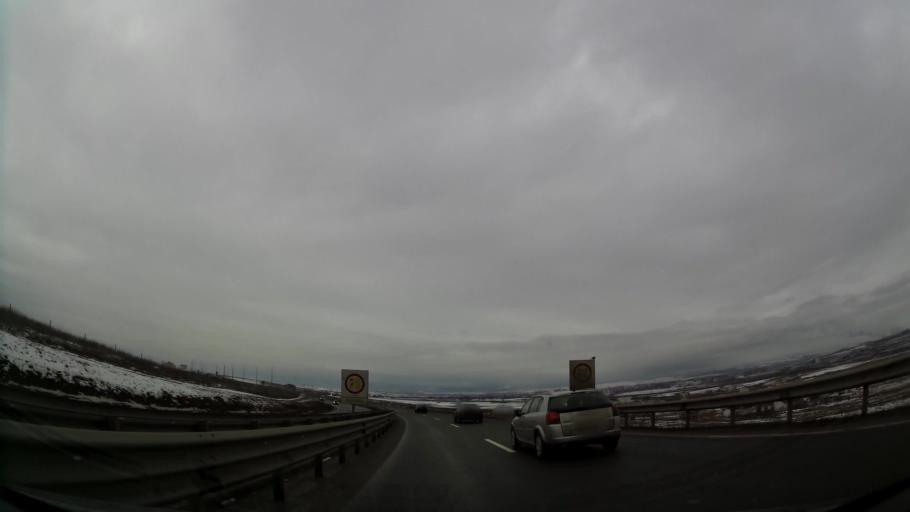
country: XK
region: Pristina
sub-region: Komuna e Prishtines
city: Pristina
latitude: 42.6321
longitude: 21.1396
